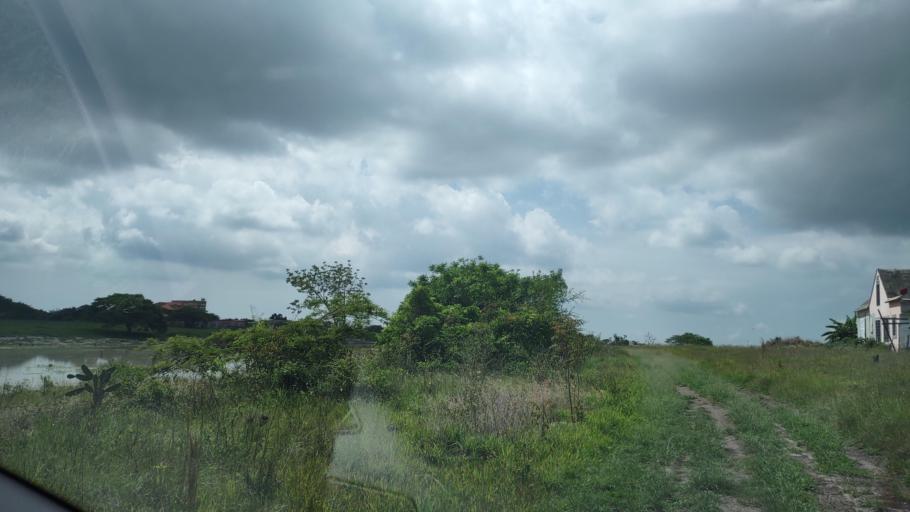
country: MX
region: Veracruz
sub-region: Emiliano Zapata
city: Dos Rios
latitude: 19.4620
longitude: -96.7965
